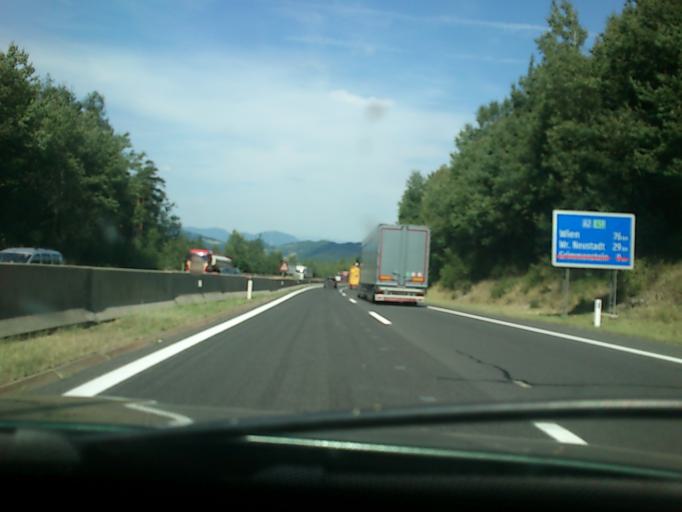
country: AT
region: Lower Austria
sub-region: Politischer Bezirk Neunkirchen
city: Thomasberg
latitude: 47.5575
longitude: 16.1271
